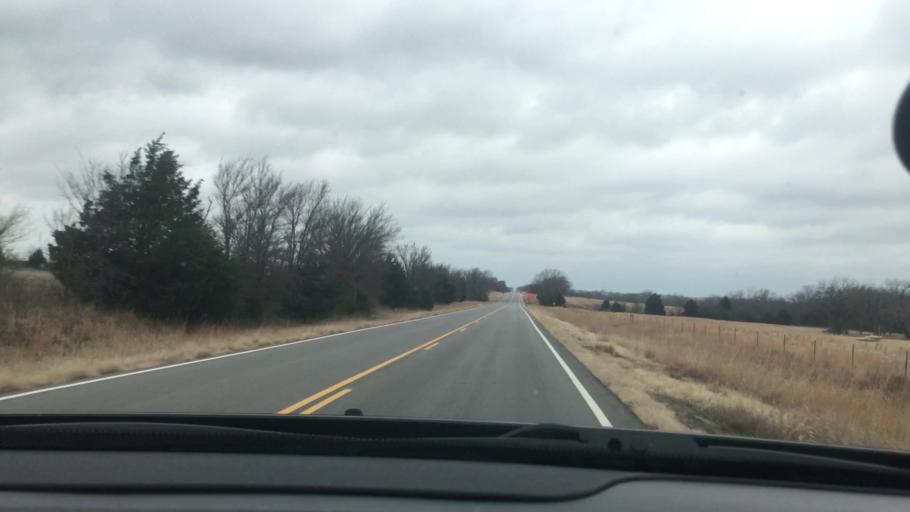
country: US
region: Oklahoma
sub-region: Atoka County
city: Atoka
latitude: 34.3749
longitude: -96.1988
